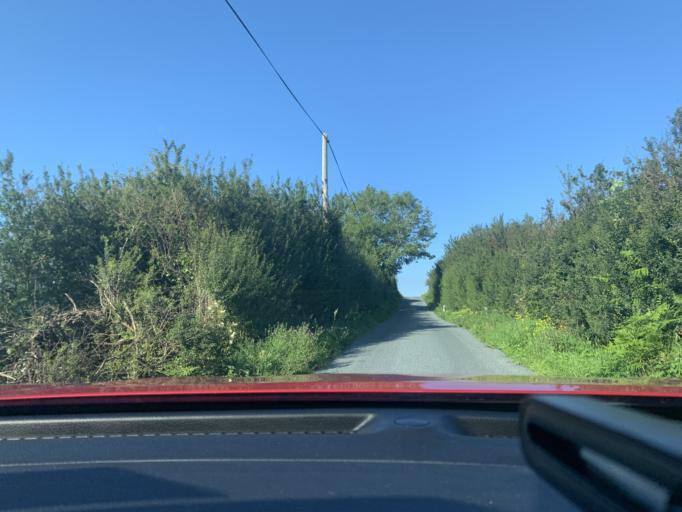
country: IE
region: Connaught
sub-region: Sligo
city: Tobercurry
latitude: 54.1469
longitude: -8.6778
